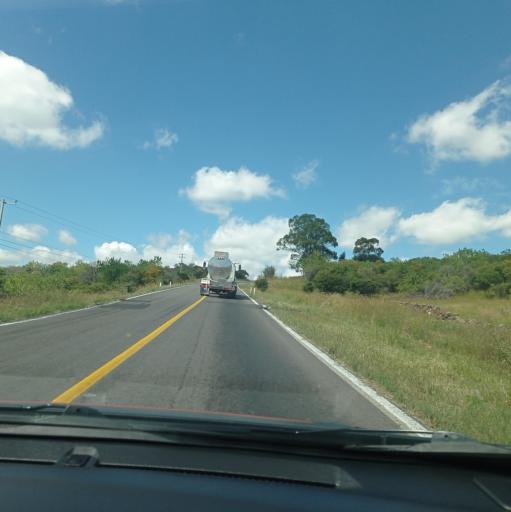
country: MX
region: Jalisco
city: Valle de Guadalupe
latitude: 21.0188
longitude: -102.5240
